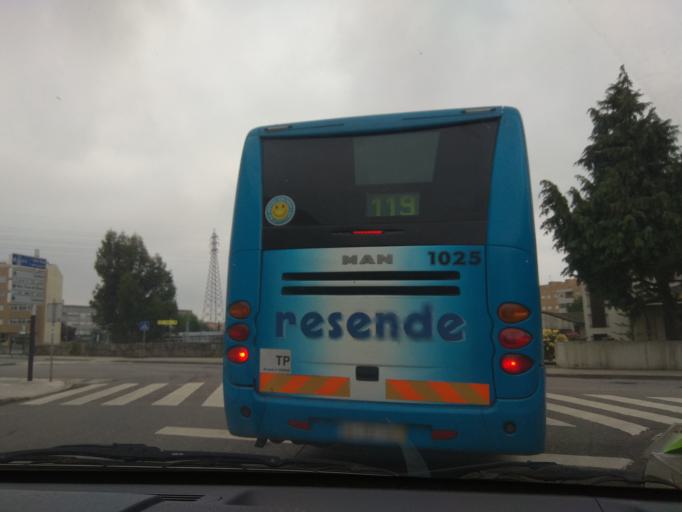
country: PT
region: Porto
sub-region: Matosinhos
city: Senhora da Hora
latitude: 41.1923
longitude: -8.6599
